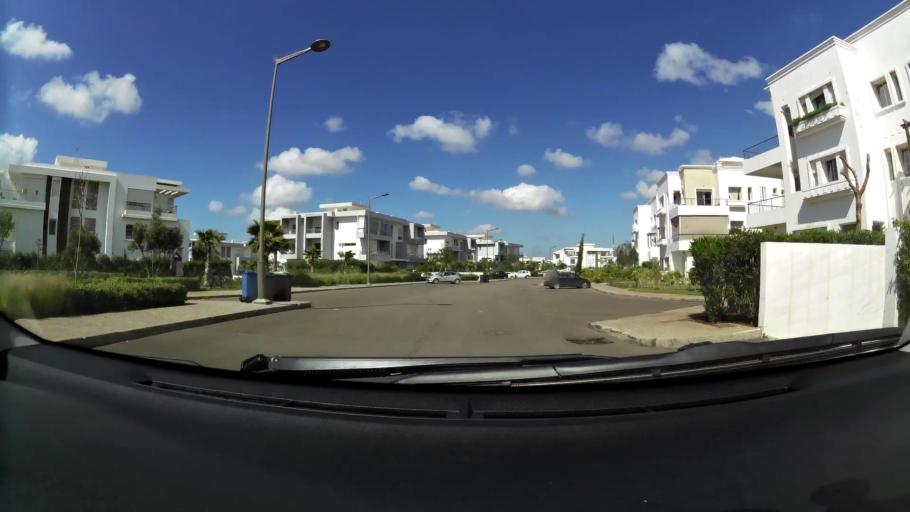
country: MA
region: Grand Casablanca
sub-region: Nouaceur
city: Bouskoura
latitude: 33.4708
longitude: -7.6043
